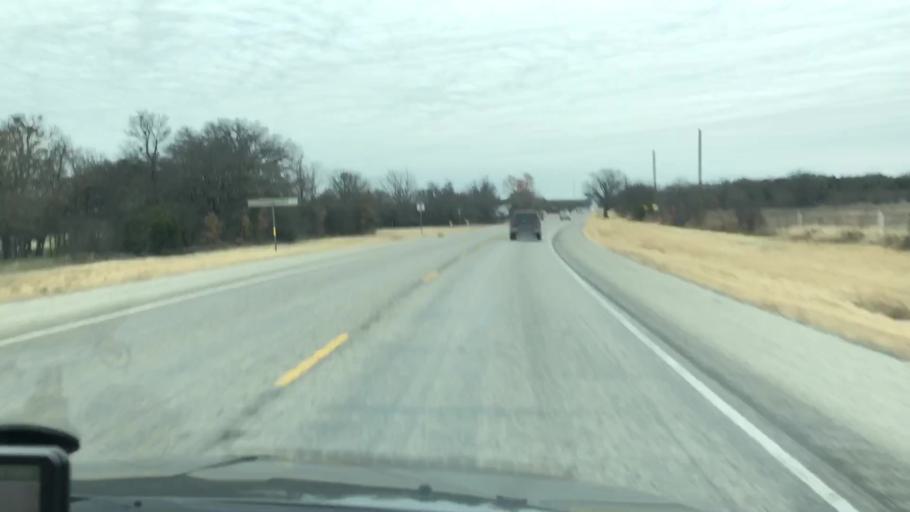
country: US
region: Texas
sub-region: Palo Pinto County
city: Mineral Wells
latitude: 32.8904
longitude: -98.0880
